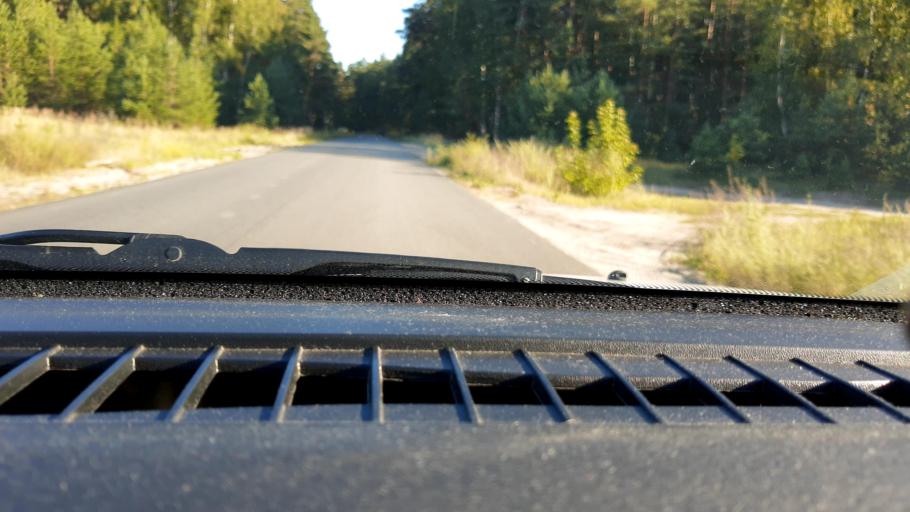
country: RU
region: Nizjnij Novgorod
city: Babino
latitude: 56.3337
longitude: 43.6186
